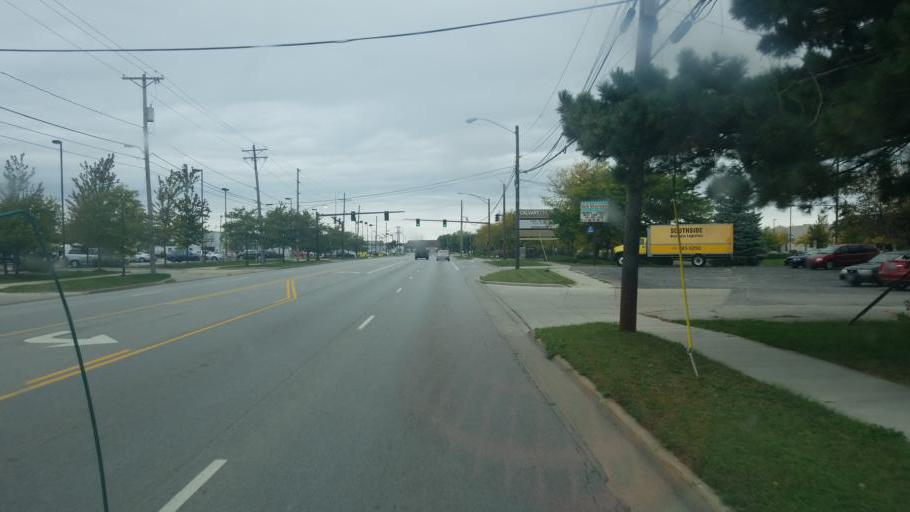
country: US
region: Ohio
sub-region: Lucas County
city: Maumee
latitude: 41.5746
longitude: -83.6602
